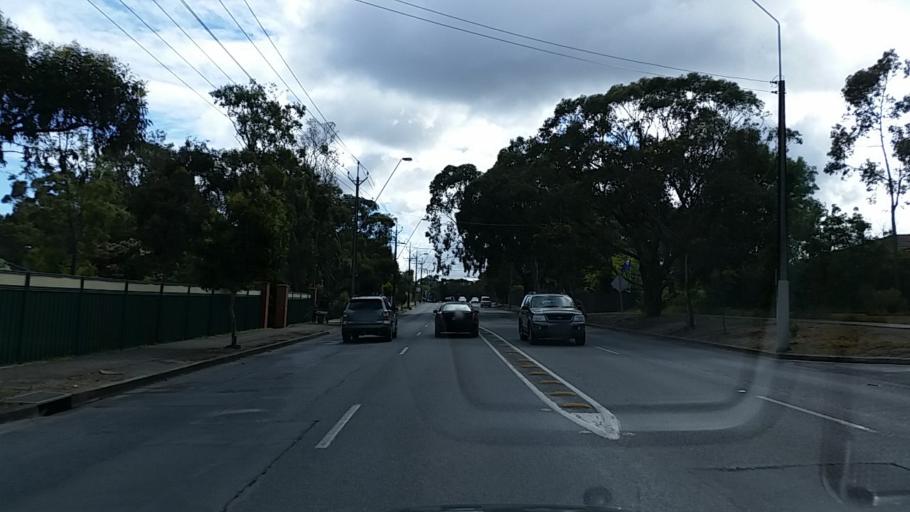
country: AU
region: South Australia
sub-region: Mitcham
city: Blackwood
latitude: -35.0251
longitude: 138.6051
